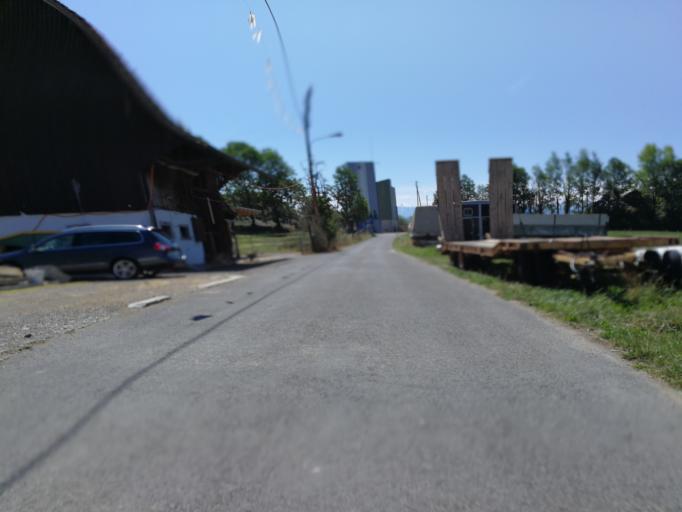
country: CH
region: Zurich
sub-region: Bezirk Hinwil
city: Gossau
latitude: 47.3151
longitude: 8.7511
